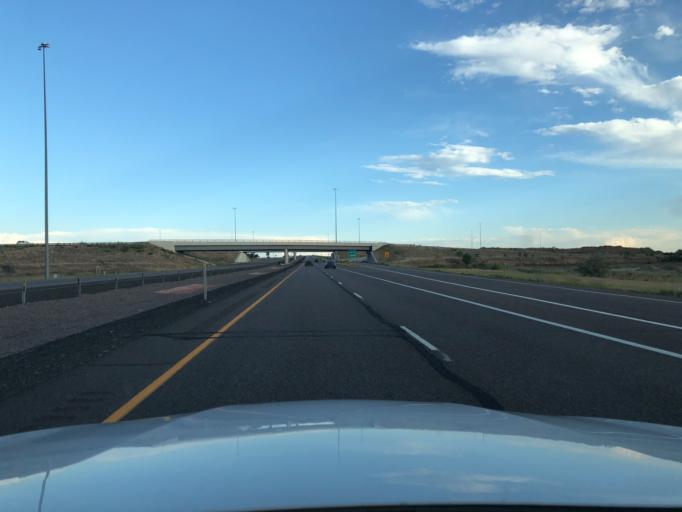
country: US
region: Colorado
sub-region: Adams County
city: Todd Creek
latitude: 39.9437
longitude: -104.8542
